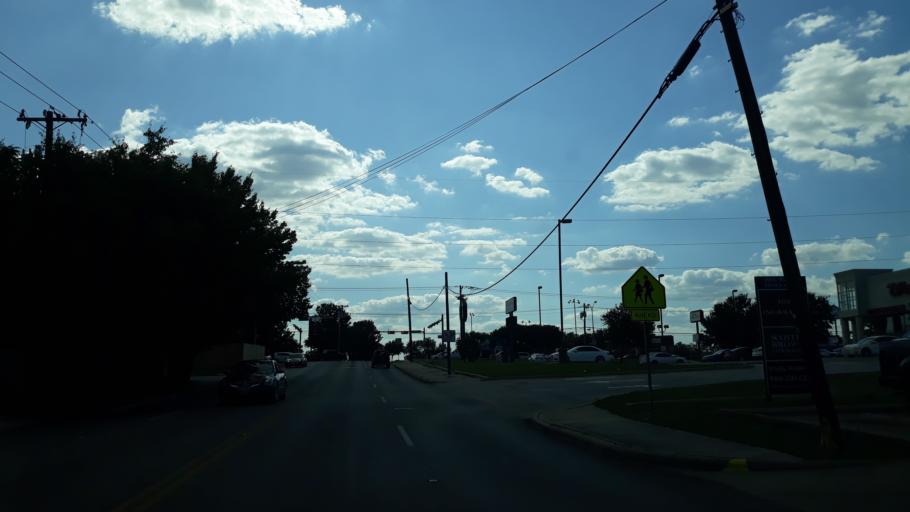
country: US
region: Texas
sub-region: Dallas County
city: Irving
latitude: 32.8509
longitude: -96.9908
